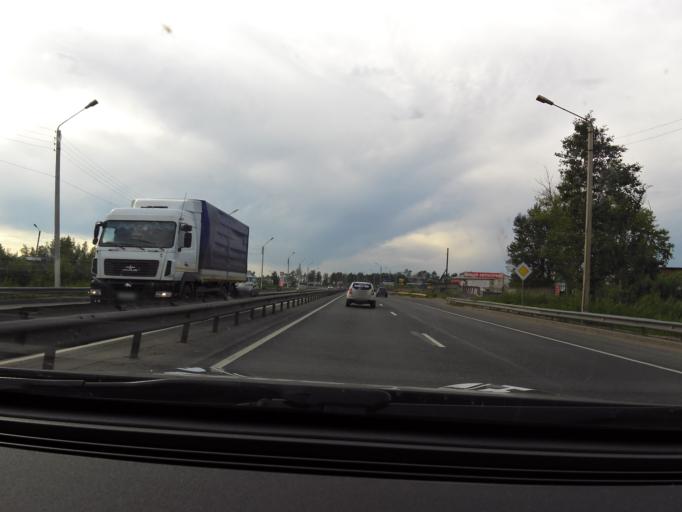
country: RU
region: Vladimir
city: Vyazniki
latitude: 56.2368
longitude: 42.1092
